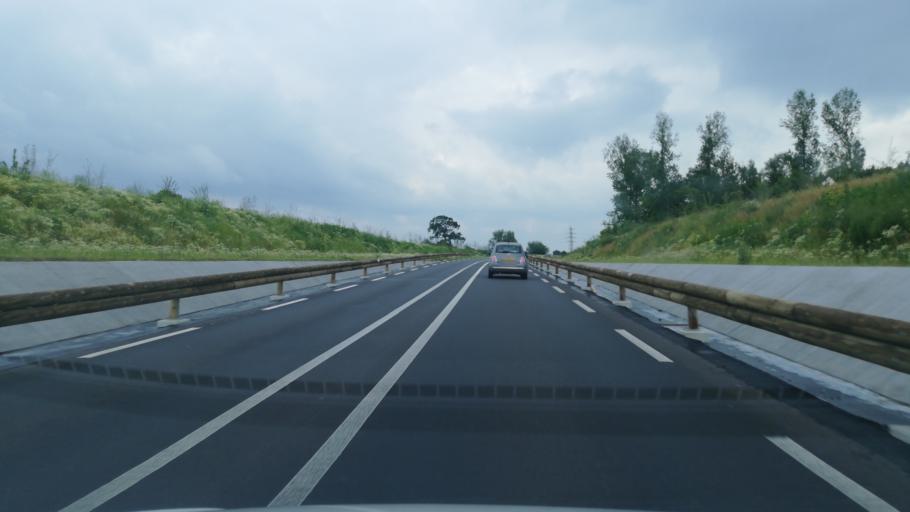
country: NL
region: Gelderland
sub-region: Gemeente Voorst
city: Voorst
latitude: 52.1664
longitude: 6.1339
